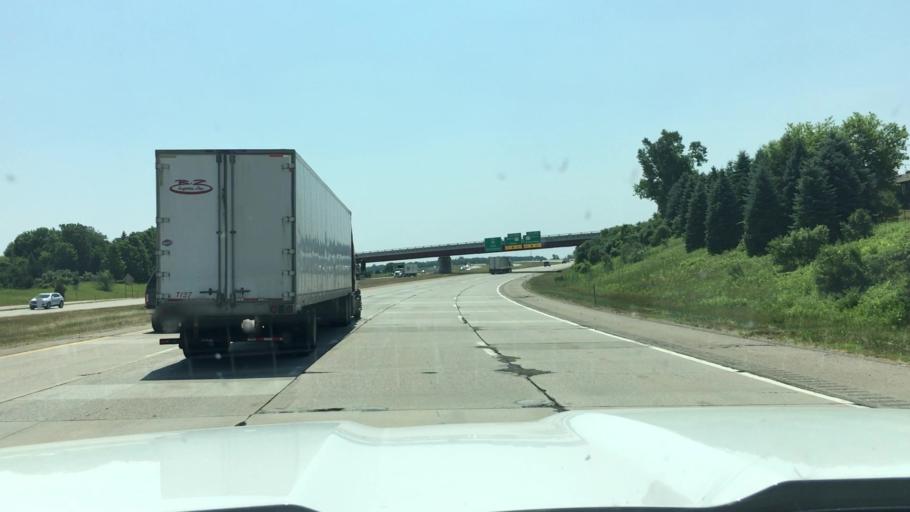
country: US
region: Michigan
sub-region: Clinton County
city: DeWitt
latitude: 42.8148
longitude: -84.5201
